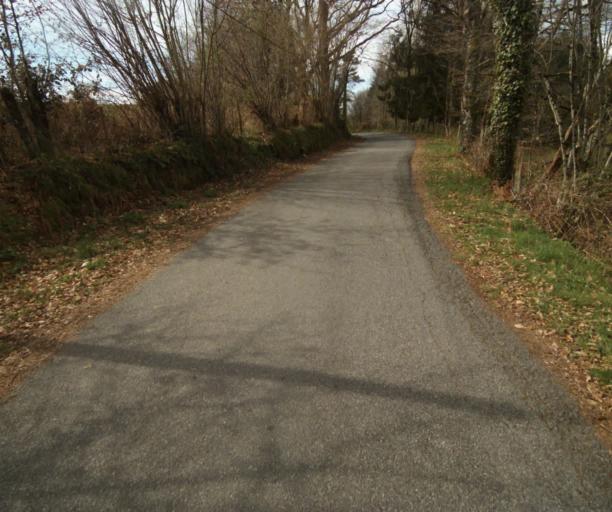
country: FR
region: Limousin
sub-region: Departement de la Correze
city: Correze
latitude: 45.3931
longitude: 1.8998
